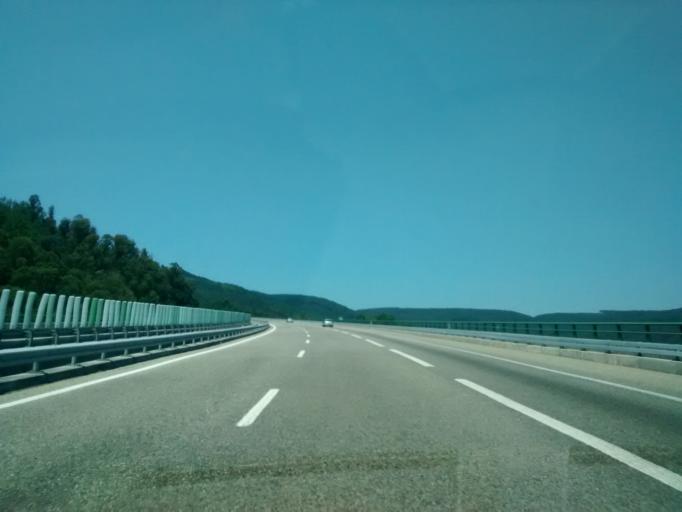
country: PT
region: Viana do Castelo
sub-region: Ponte de Lima
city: Ponte de Lima
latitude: 41.8393
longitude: -8.6025
